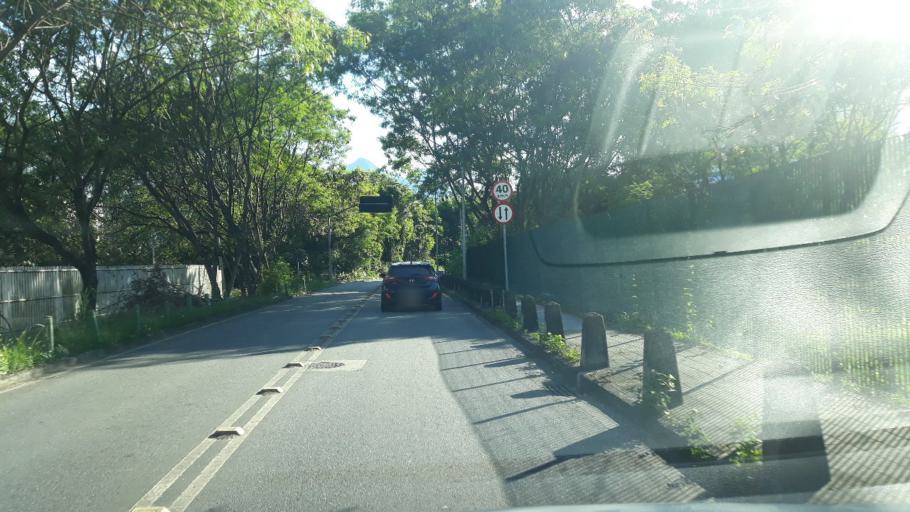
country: BR
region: Rio de Janeiro
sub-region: Rio De Janeiro
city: Rio de Janeiro
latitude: -22.9969
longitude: -43.3543
